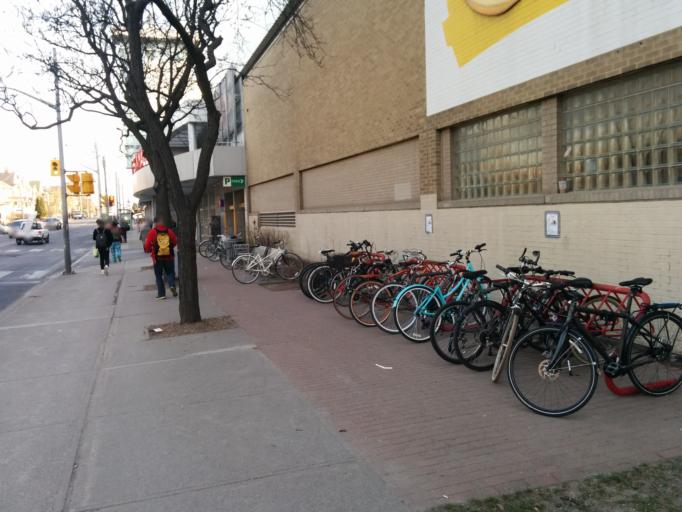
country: CA
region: Ontario
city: Toronto
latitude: 43.6554
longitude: -79.4339
